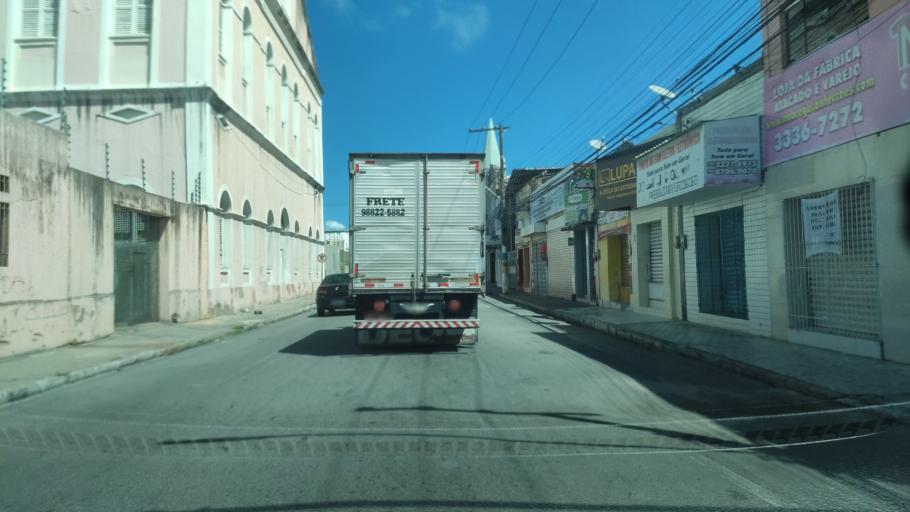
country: BR
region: Alagoas
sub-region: Maceio
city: Maceio
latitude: -9.6646
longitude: -35.7421
